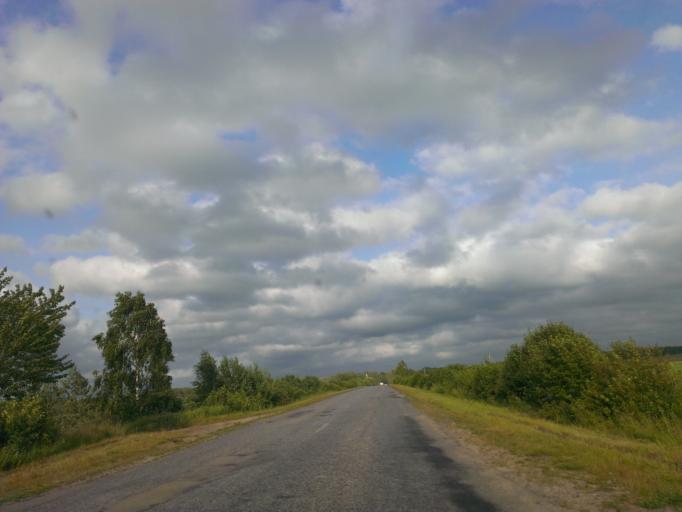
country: LV
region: Aizpute
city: Aizpute
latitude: 56.7324
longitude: 21.7067
